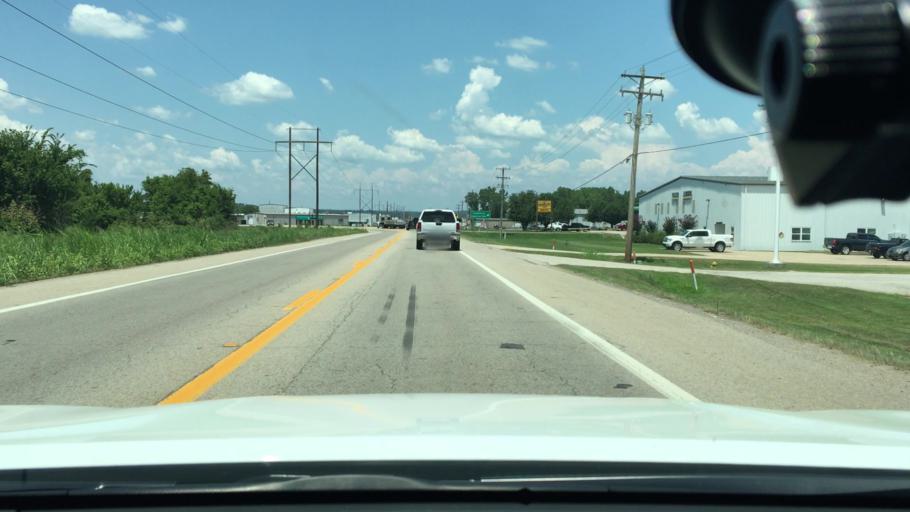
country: US
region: Arkansas
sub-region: Crawford County
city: Van Buren
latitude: 35.4115
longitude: -94.3298
